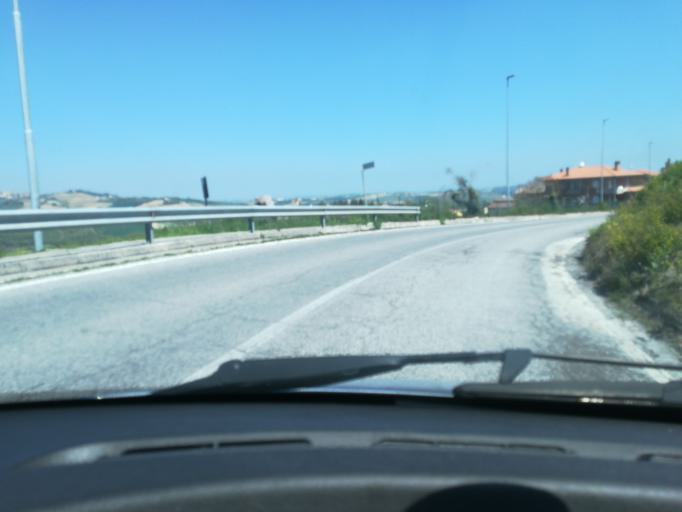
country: IT
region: The Marches
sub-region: Provincia di Macerata
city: Strada
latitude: 43.3959
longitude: 13.2055
